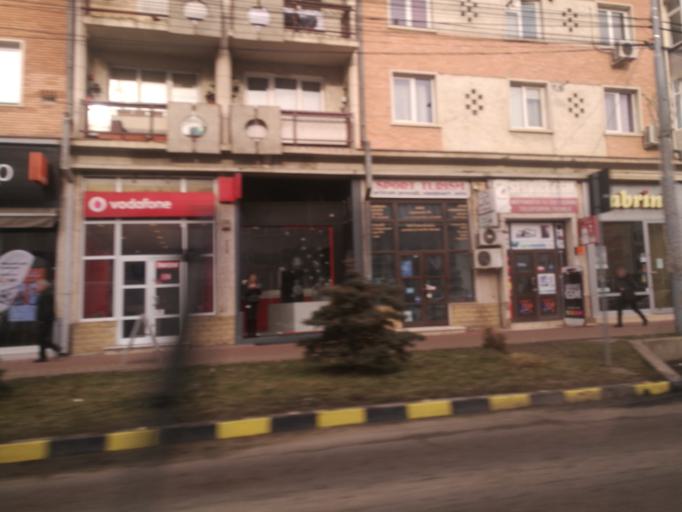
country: RO
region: Suceava
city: Suceava
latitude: 47.6452
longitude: 26.2591
